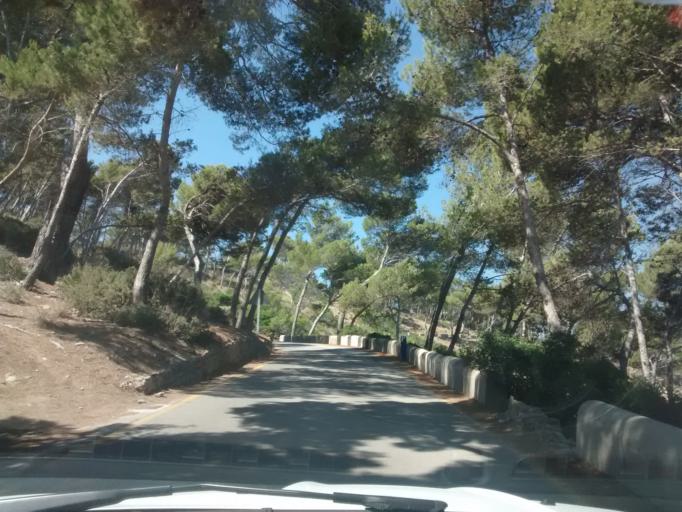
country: ES
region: Balearic Islands
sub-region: Illes Balears
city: Port d'Alcudia
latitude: 39.8720
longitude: 3.1606
